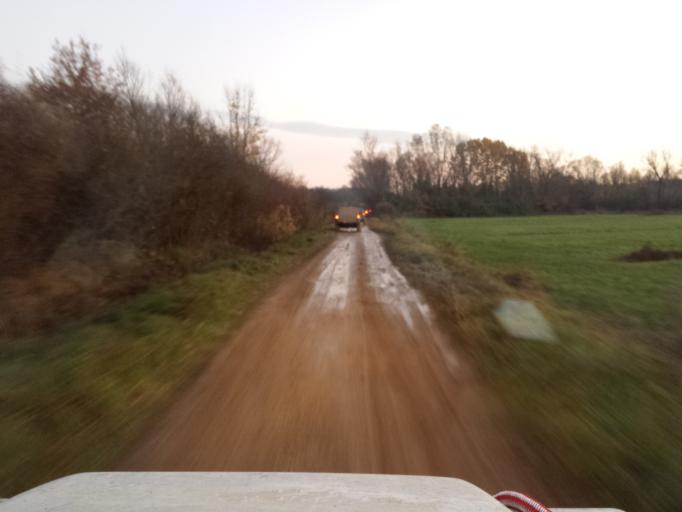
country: IT
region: Friuli Venezia Giulia
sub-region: Provincia di Gorizia
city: Capriva del Friuli
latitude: 45.9665
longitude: 13.5142
